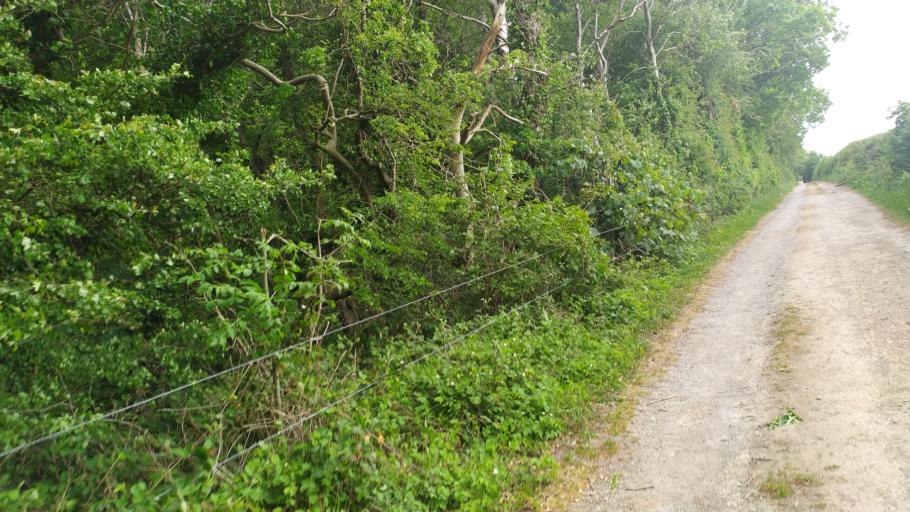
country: GB
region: England
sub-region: City and Borough of Leeds
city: Thorner
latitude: 53.8594
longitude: -1.3916
